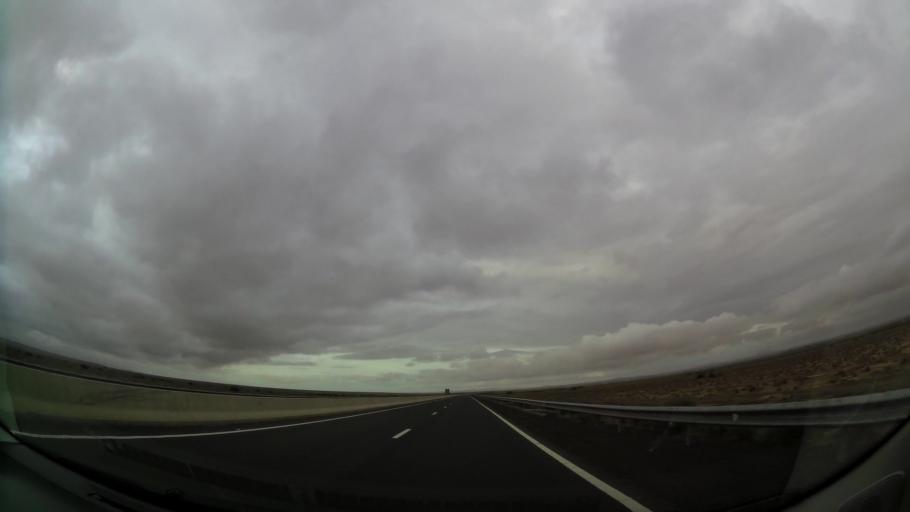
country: MA
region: Taza-Al Hoceima-Taounate
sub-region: Taza
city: Guercif
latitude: 34.3721
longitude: -3.2667
